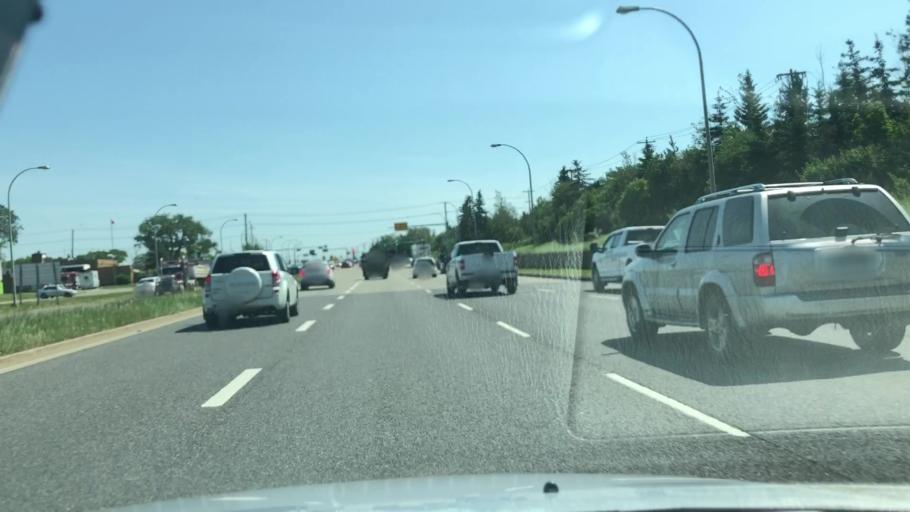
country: CA
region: Alberta
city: Edmonton
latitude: 53.5807
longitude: -113.5452
